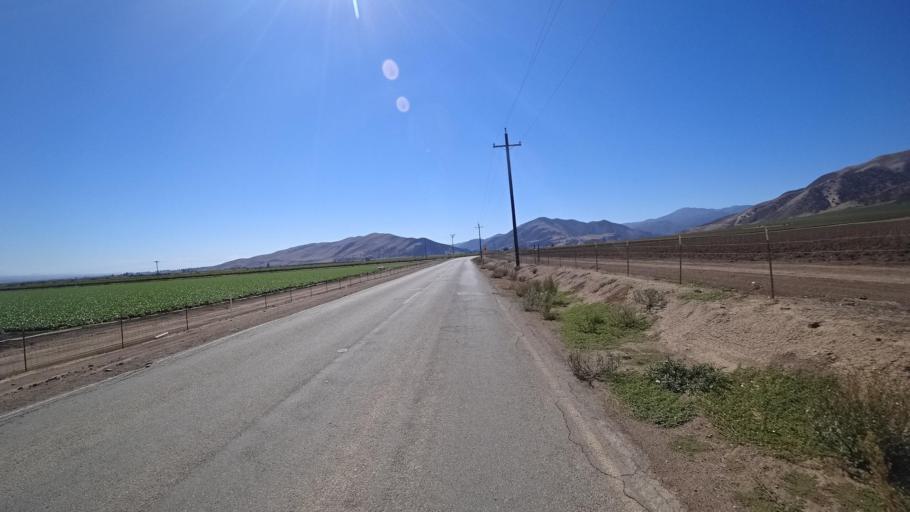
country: US
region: California
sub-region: Monterey County
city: Greenfield
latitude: 36.3148
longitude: -121.3122
